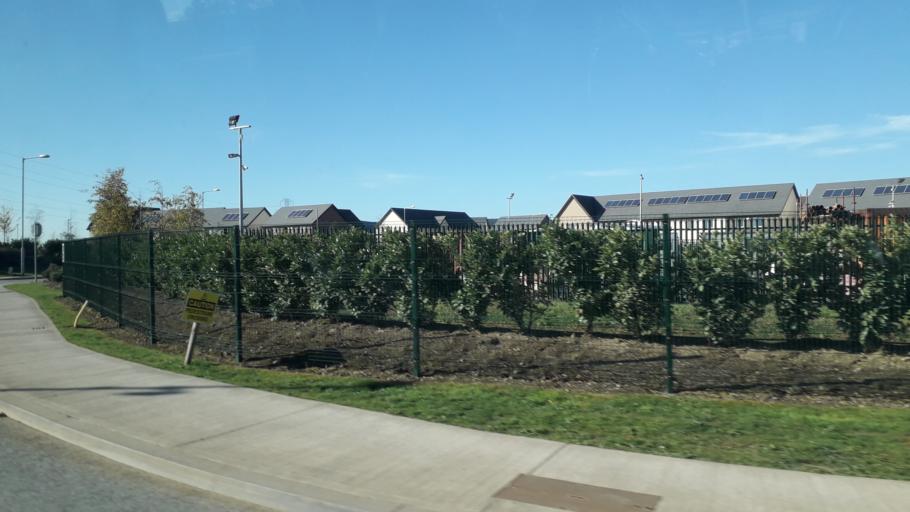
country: IE
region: Leinster
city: Hartstown
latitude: 53.3907
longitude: -6.4398
